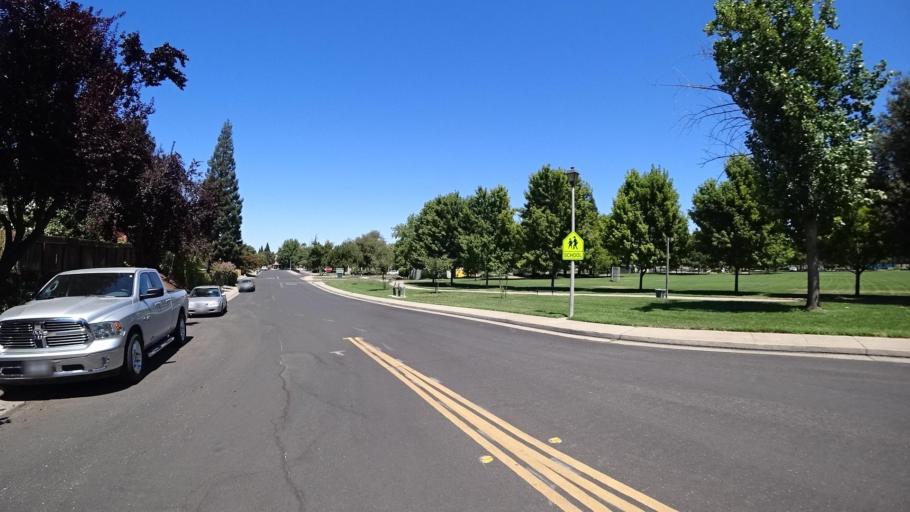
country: US
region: California
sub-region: Placer County
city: Rocklin
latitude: 38.8082
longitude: -121.2643
